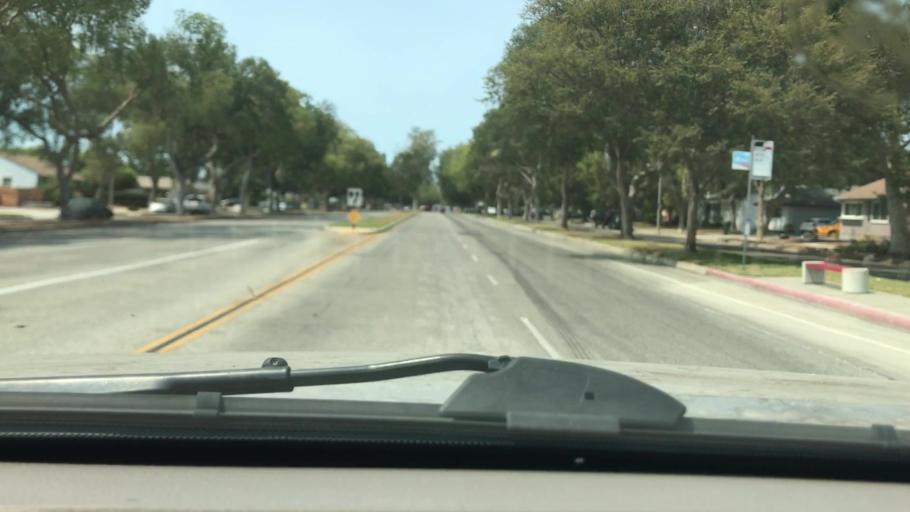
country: US
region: California
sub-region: Orange County
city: Rossmoor
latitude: 33.7924
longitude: -118.0993
